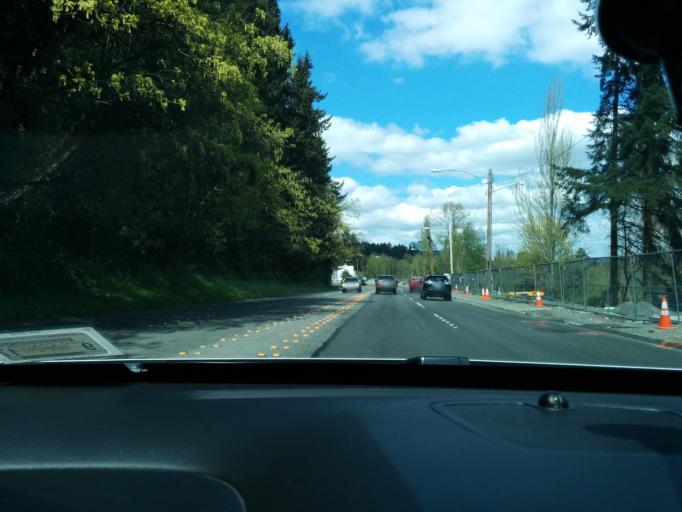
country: US
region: Washington
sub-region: King County
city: Newport
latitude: 47.5884
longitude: -122.1919
